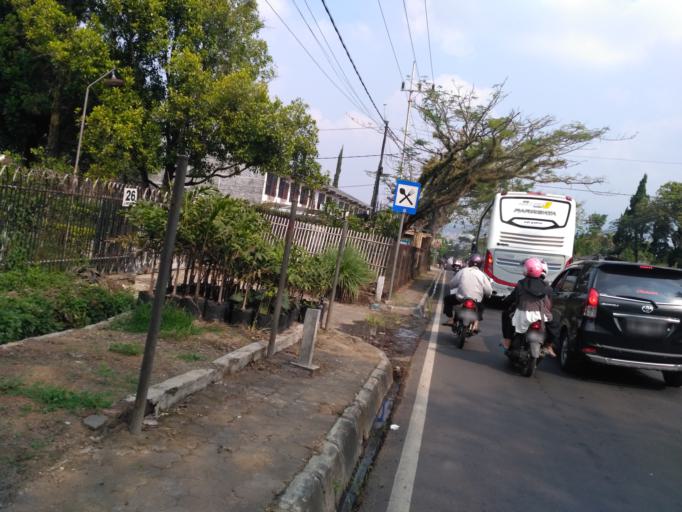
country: ID
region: East Java
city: Batu
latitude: -7.8578
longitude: 112.5269
